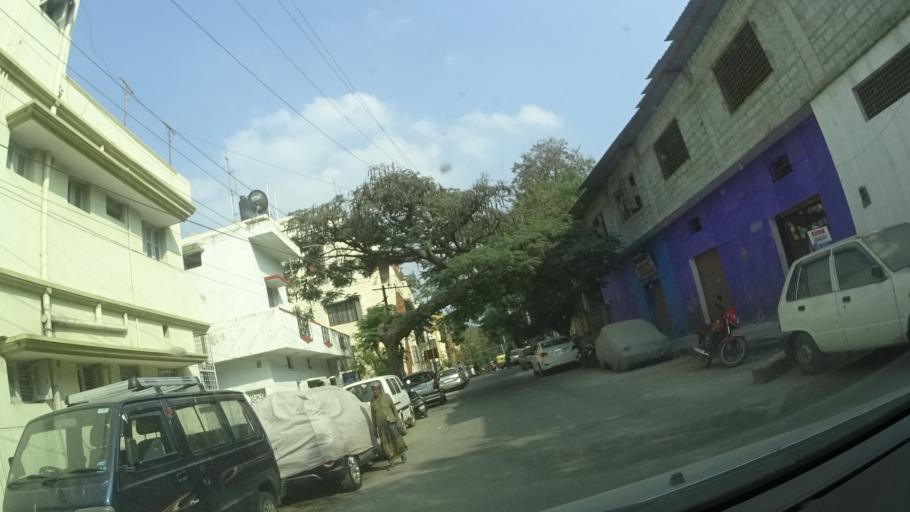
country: IN
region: Karnataka
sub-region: Bangalore Urban
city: Bangalore
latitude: 12.9496
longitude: 77.5598
